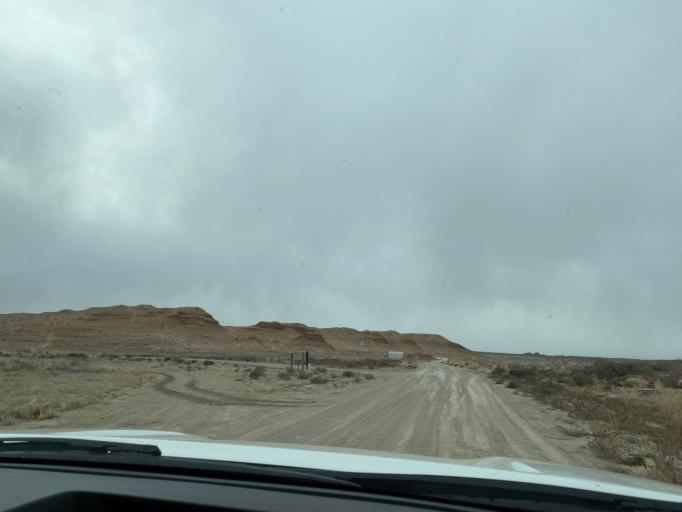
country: US
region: Utah
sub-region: Emery County
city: Ferron
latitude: 38.3682
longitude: -110.7122
